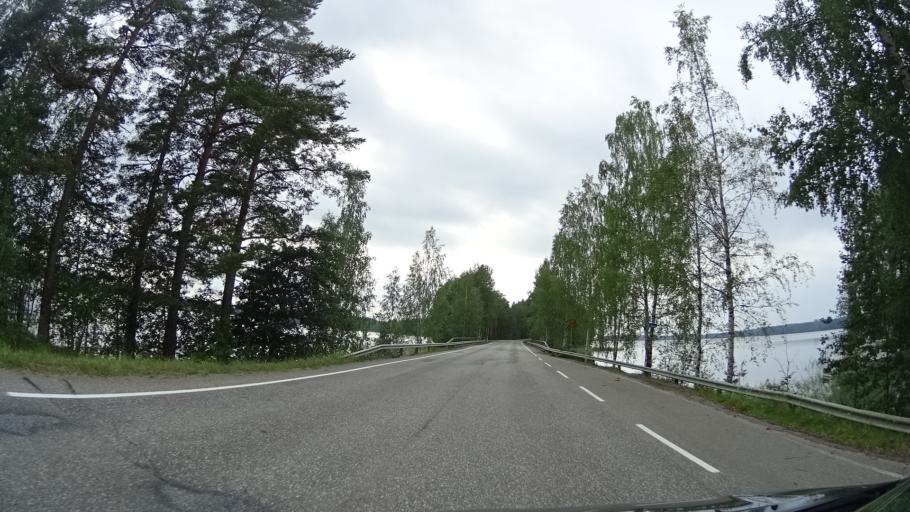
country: FI
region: Southern Savonia
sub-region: Savonlinna
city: Punkaharju
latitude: 61.7515
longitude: 29.4334
